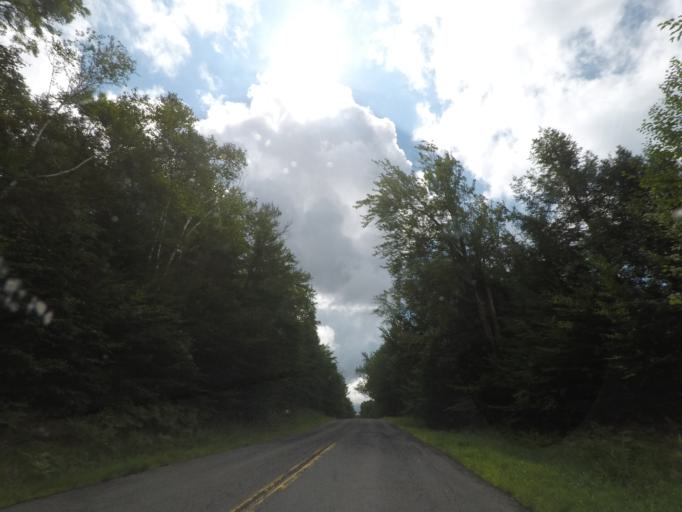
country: US
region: New York
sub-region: Rensselaer County
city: Averill Park
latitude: 42.6764
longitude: -73.4242
